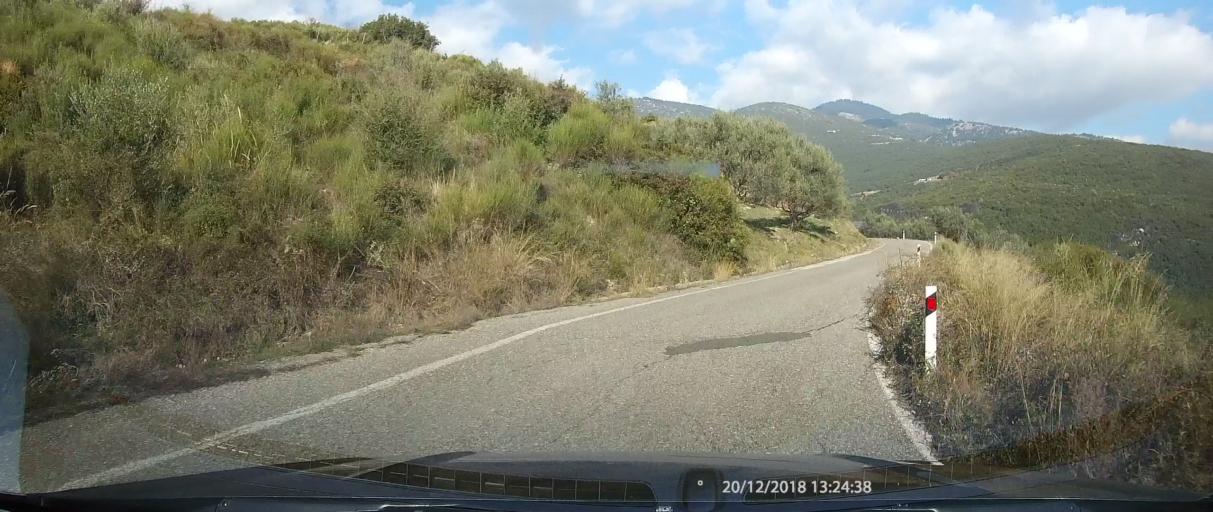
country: GR
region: West Greece
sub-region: Nomos Aitolias kai Akarnanias
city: Paravola
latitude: 38.6199
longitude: 21.5674
